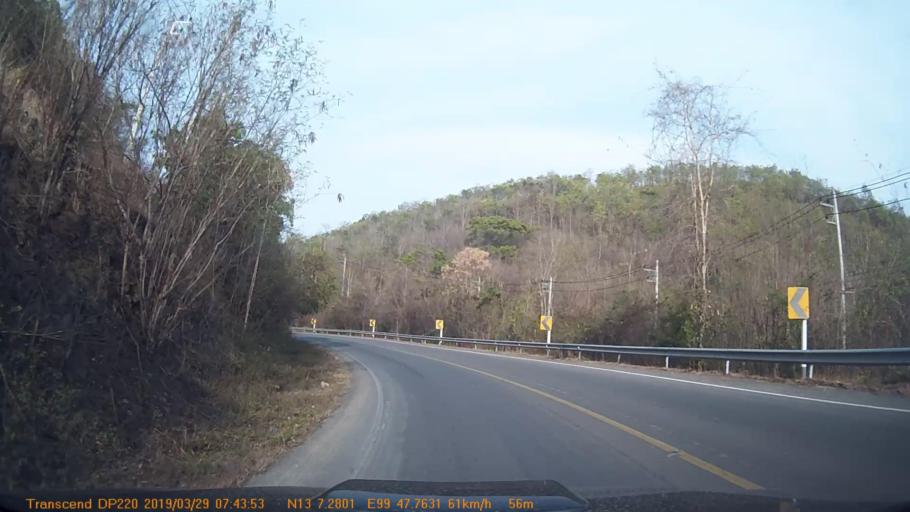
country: TH
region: Phetchaburi
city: Nong Ya Plong
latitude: 13.1214
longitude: 99.7959
